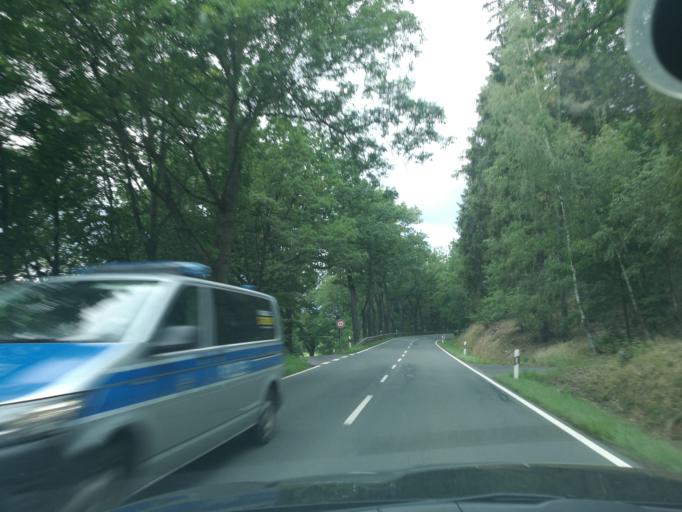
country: DE
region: Saxony
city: Eichigt
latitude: 50.3717
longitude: 12.2094
